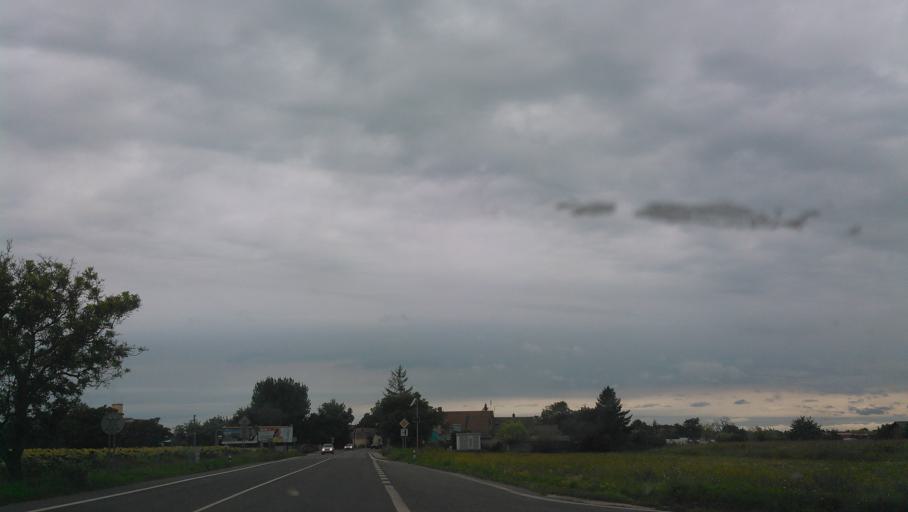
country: SK
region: Trnavsky
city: Dunajska Streda
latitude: 47.9749
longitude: 17.6657
